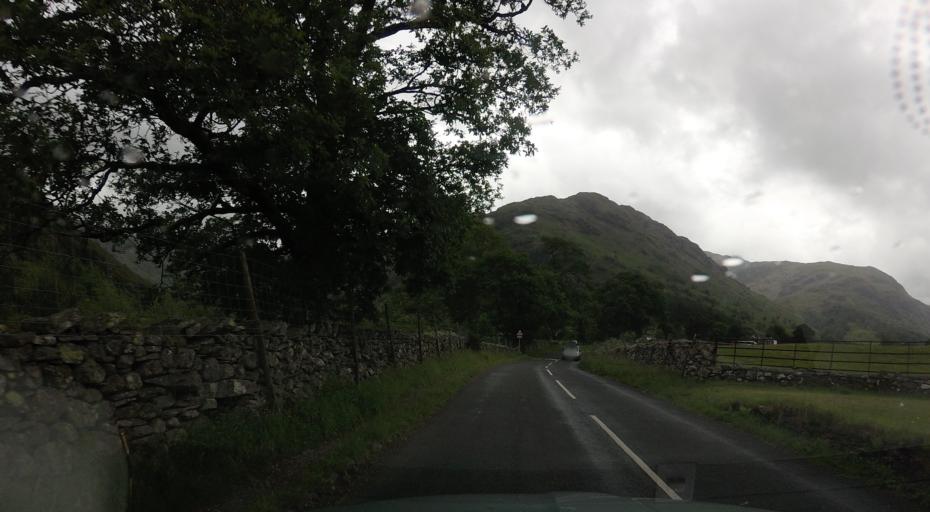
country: GB
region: England
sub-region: Cumbria
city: Keswick
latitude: 54.5203
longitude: -3.1469
